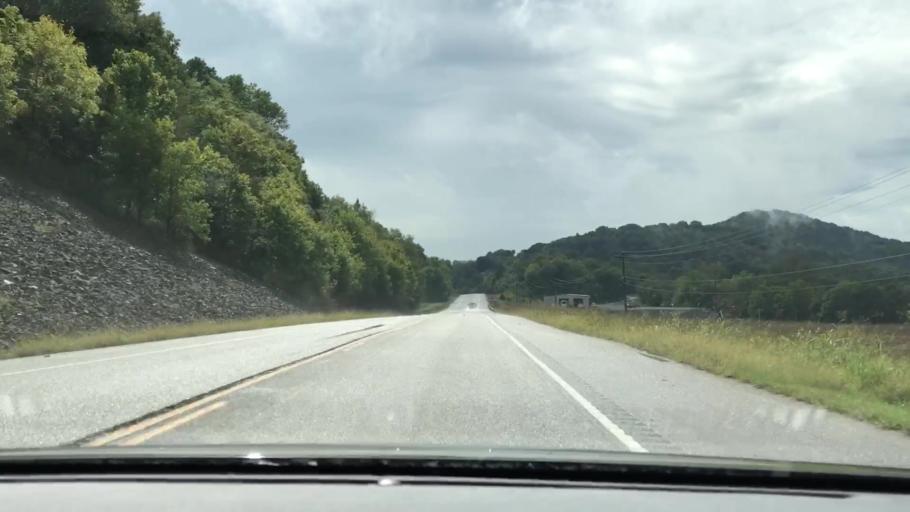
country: US
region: Tennessee
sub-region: Smith County
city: Carthage
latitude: 36.3131
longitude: -85.9711
